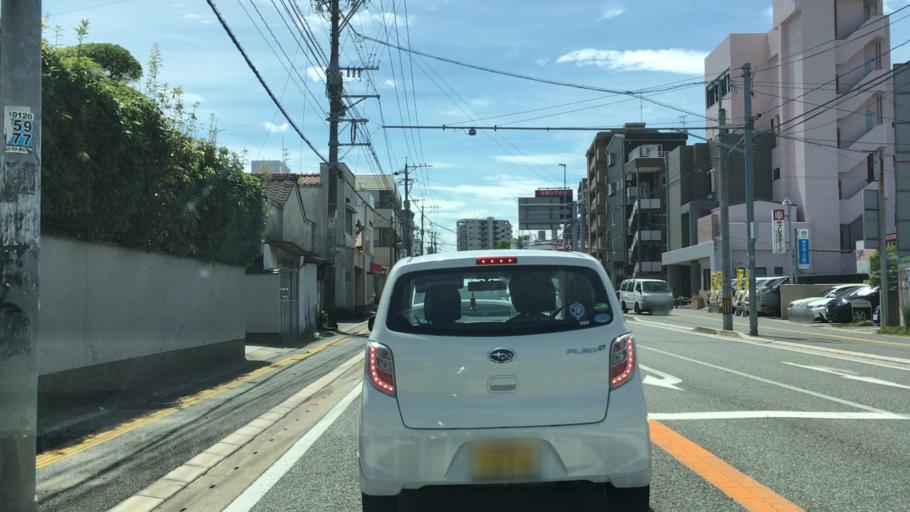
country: JP
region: Fukuoka
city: Onojo
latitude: 33.5439
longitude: 130.4715
